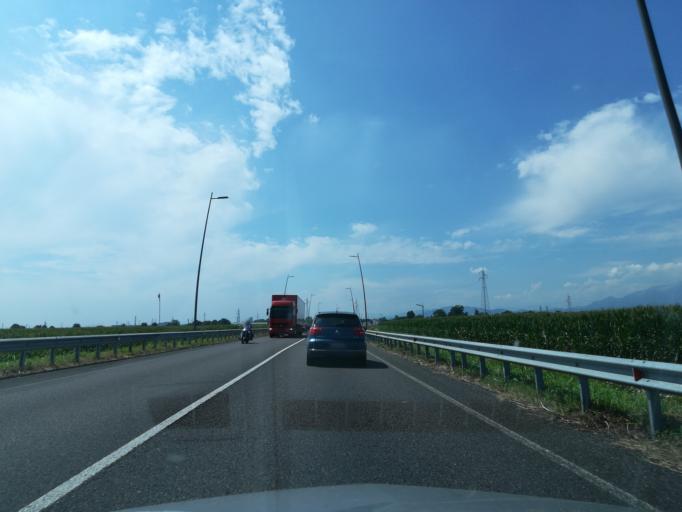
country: IT
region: Lombardy
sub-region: Provincia di Bergamo
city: Comun Nuovo
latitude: 45.6337
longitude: 9.6546
